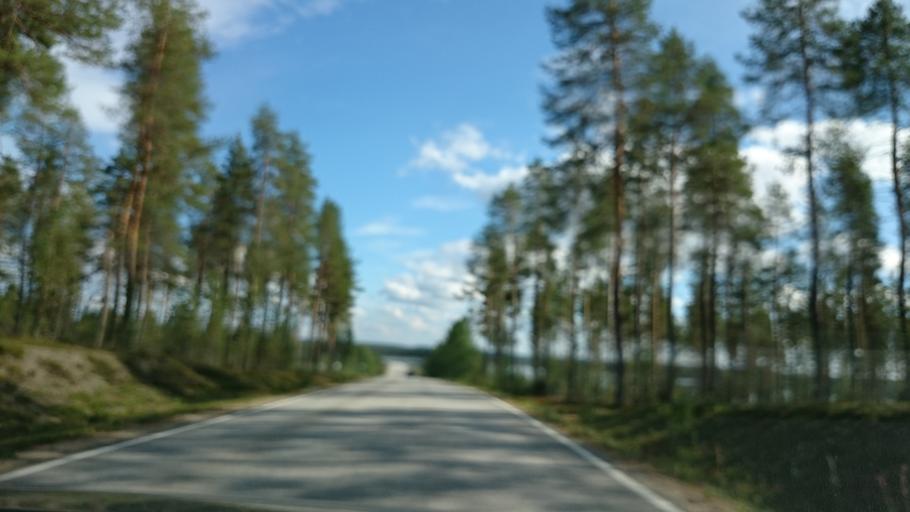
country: FI
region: Kainuu
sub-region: Kehys-Kainuu
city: Suomussalmi
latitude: 64.7660
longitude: 29.3688
